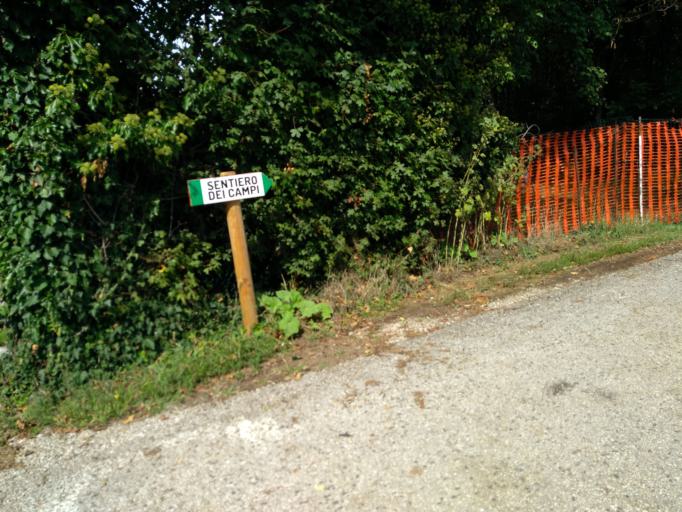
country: IT
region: Veneto
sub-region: Provincia di Vicenza
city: San Vito di Leguzzano
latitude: 45.6859
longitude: 11.3809
